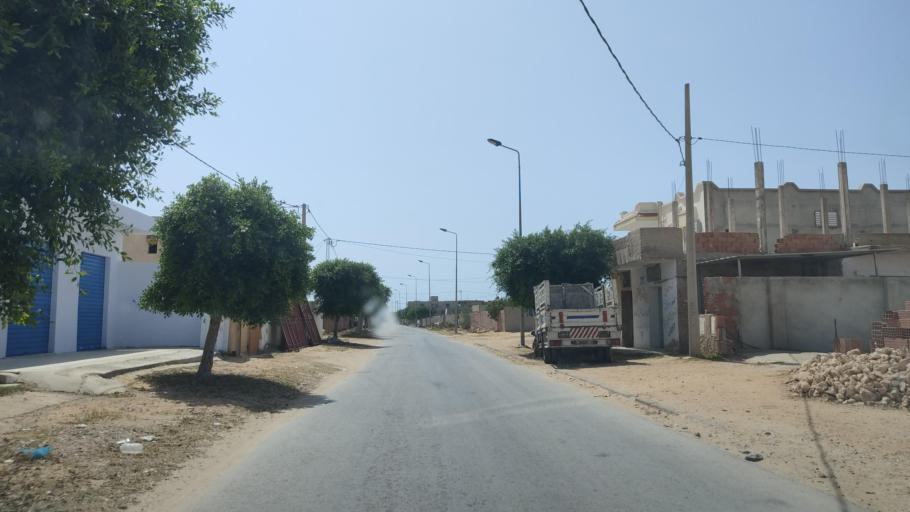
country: TN
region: Safaqis
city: Sfax
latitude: 34.6683
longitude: 10.7076
